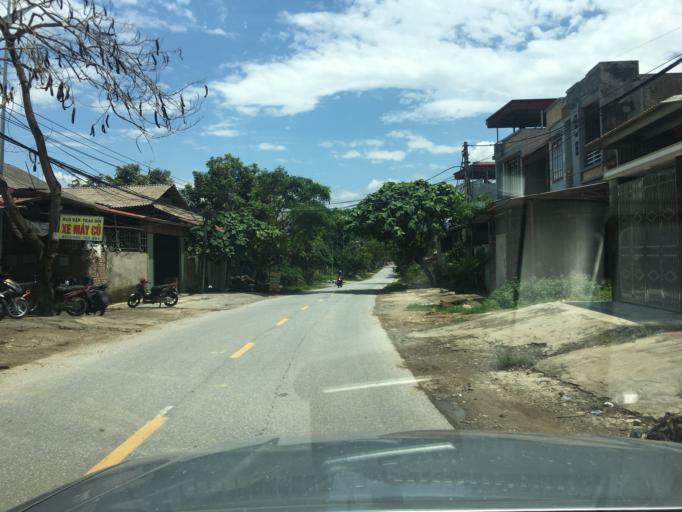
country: VN
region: Yen Bai
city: Son Thinh
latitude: 21.6167
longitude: 104.5081
